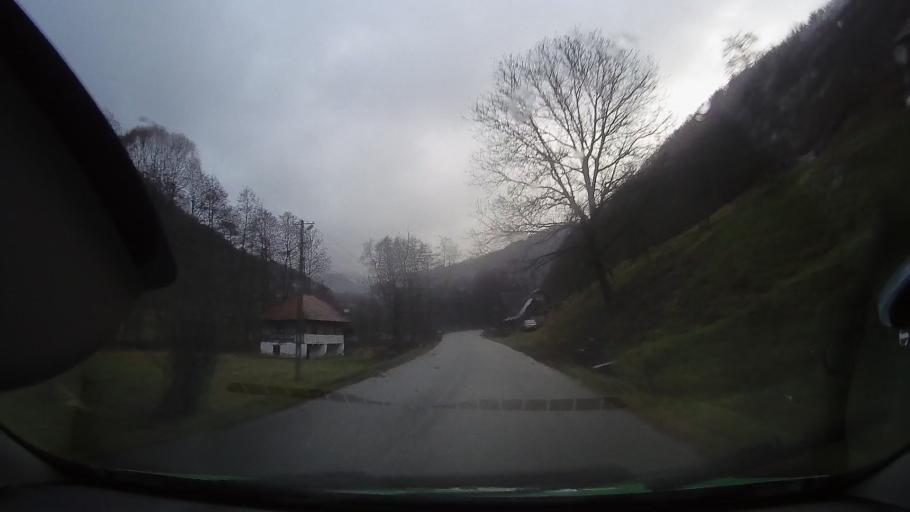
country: RO
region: Hunedoara
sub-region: Comuna Ribita
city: Ribita
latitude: 46.2726
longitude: 22.7418
